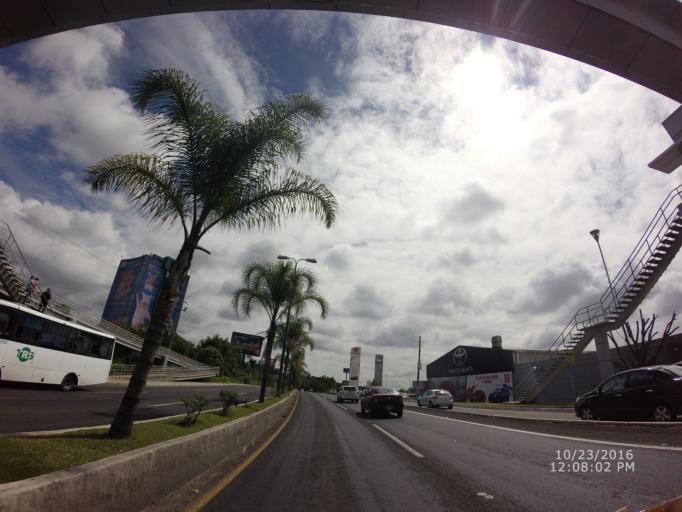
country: MX
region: Veracruz
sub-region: Xalapa
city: Colonia Santa Barbara
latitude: 19.5154
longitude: -96.8794
